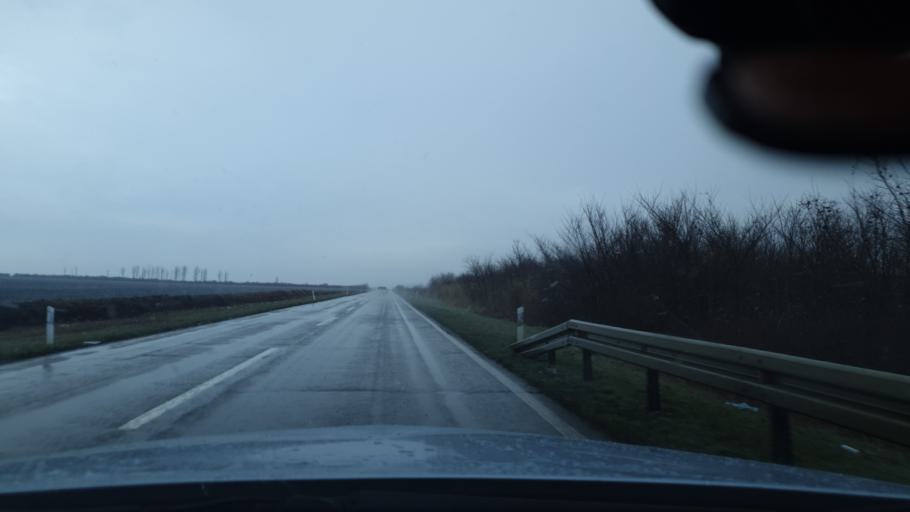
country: RS
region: Autonomna Pokrajina Vojvodina
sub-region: Juznobanatski Okrug
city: Pancevo
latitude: 44.8522
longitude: 20.7668
